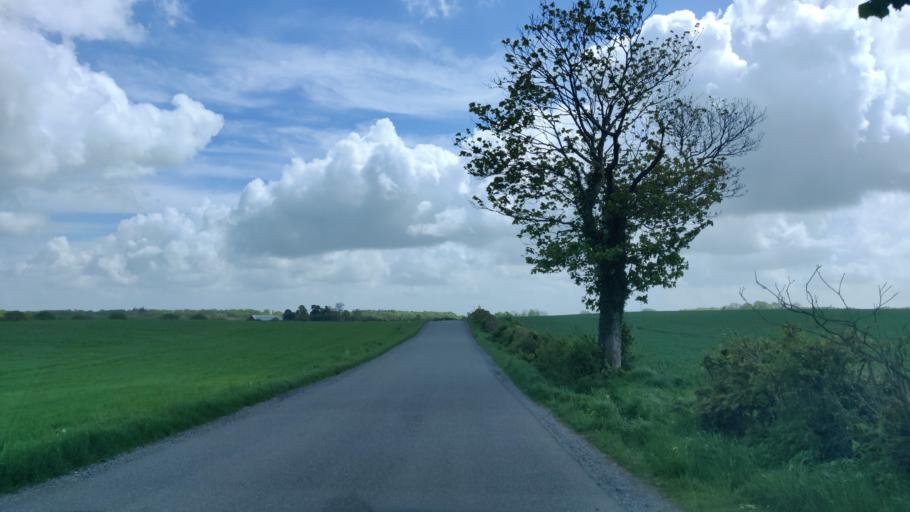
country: DK
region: South Denmark
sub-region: Vejle Kommune
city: Vejle
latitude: 55.6560
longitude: 9.5269
